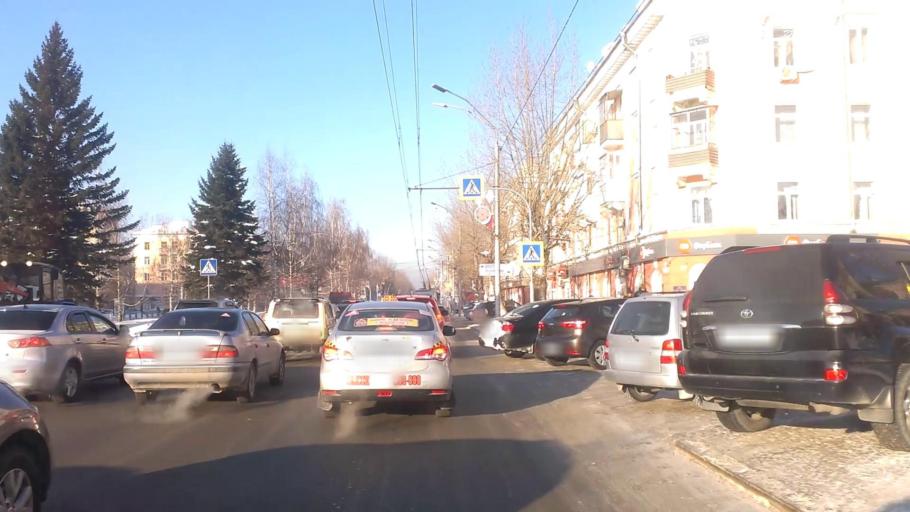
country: RU
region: Altai Krai
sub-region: Gorod Barnaulskiy
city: Barnaul
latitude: 53.3477
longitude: 83.7776
